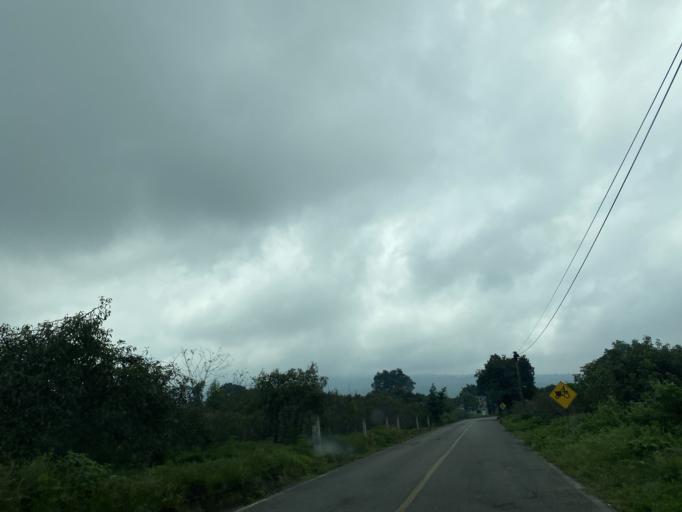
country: MX
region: Morelos
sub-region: Yecapixtla
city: Texcala
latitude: 18.9352
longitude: -98.8111
